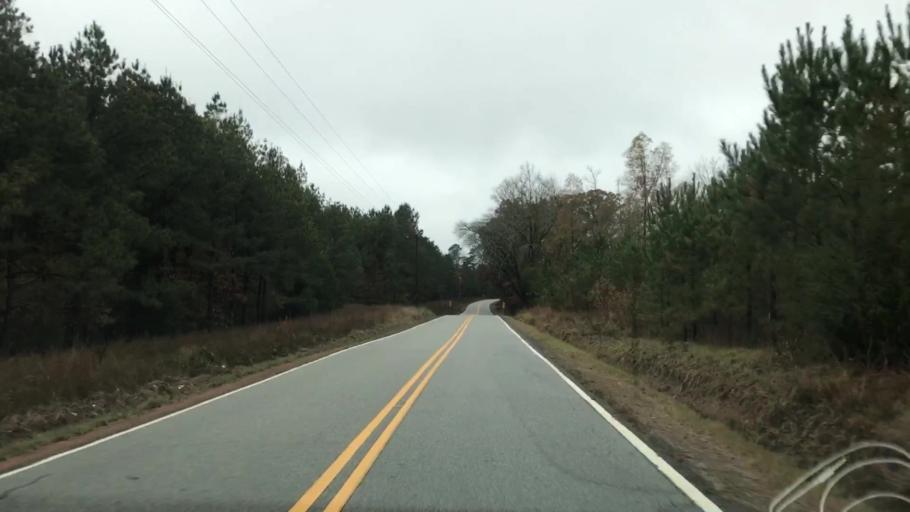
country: US
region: South Carolina
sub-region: Greenwood County
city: Ninety Six
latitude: 34.3087
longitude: -81.9540
